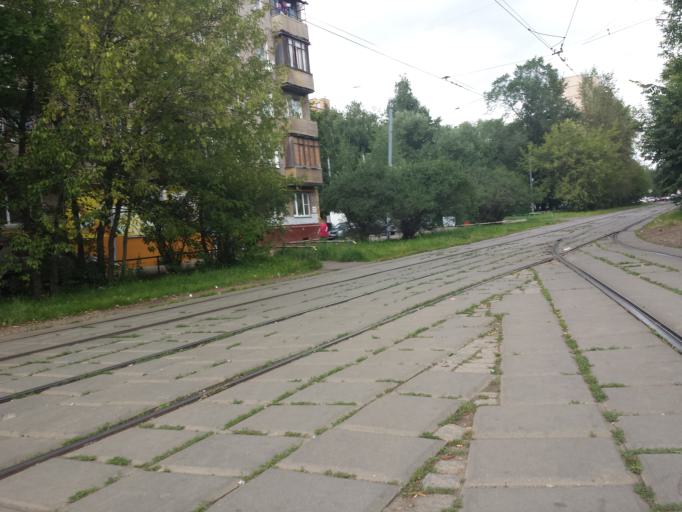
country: RU
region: Moskovskaya
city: Novogireyevo
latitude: 55.7456
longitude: 37.8170
